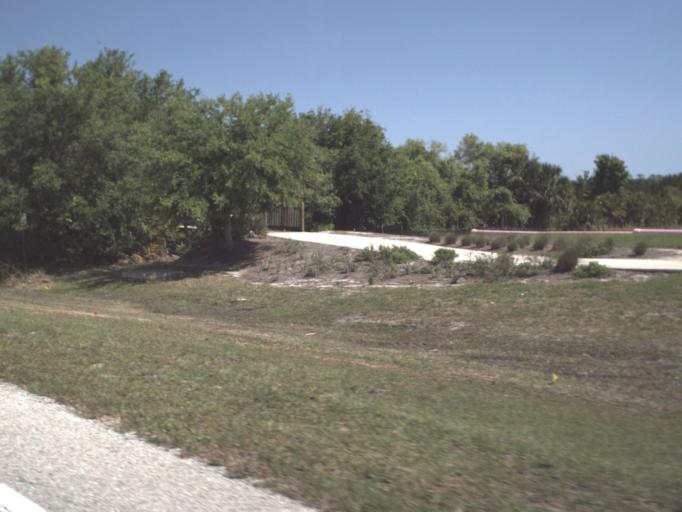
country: US
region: Florida
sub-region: Flagler County
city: Palm Coast
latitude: 29.5869
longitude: -81.2795
